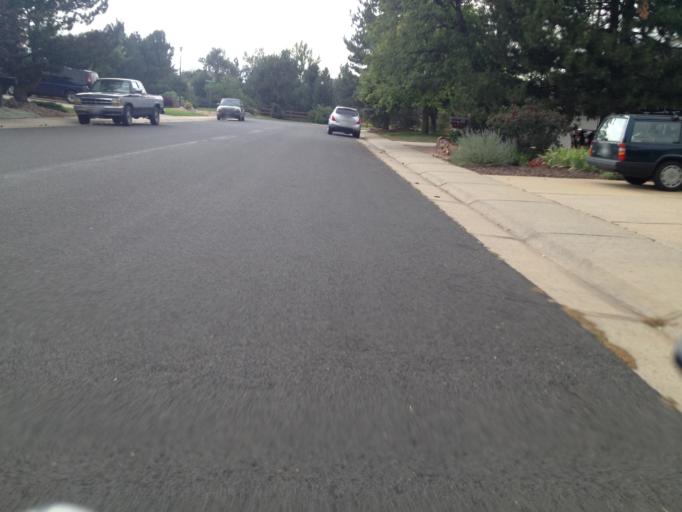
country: US
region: Colorado
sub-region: Boulder County
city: Louisville
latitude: 39.9901
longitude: -105.1620
